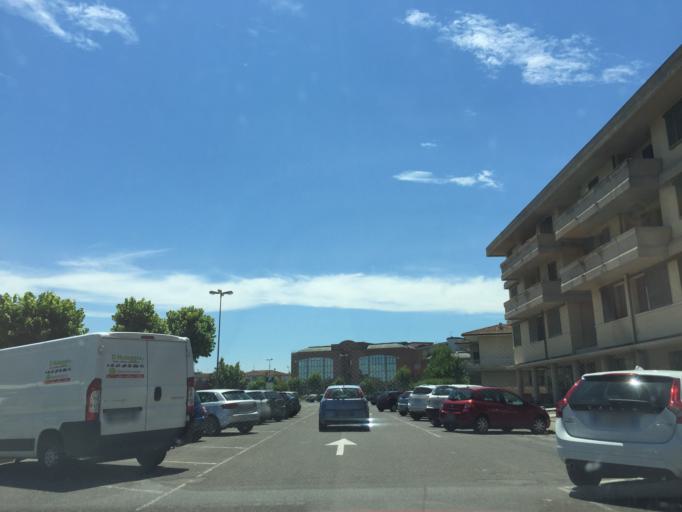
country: IT
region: Tuscany
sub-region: Province of Pisa
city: San Miniato
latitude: 43.6859
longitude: 10.7983
